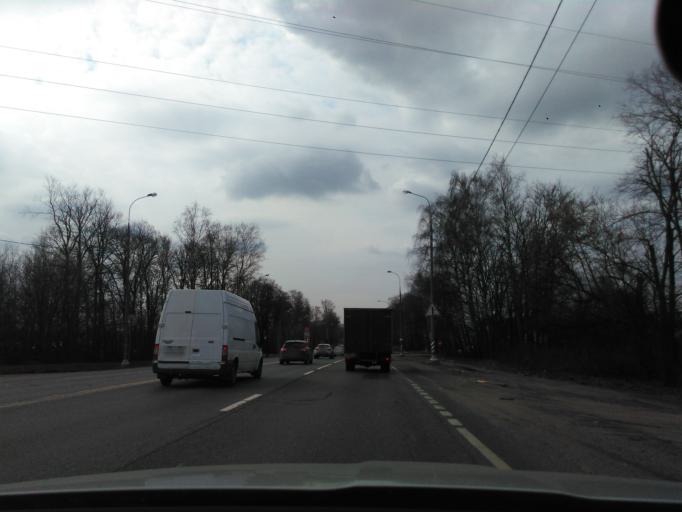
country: RU
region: Moskovskaya
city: Sheremet'yevskiy
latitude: 55.9896
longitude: 37.5315
